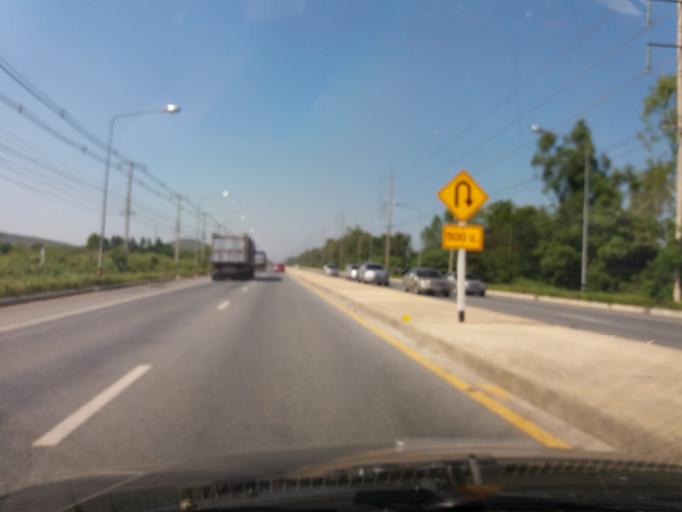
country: TH
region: Chai Nat
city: Chai Nat
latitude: 15.2322
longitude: 100.1075
